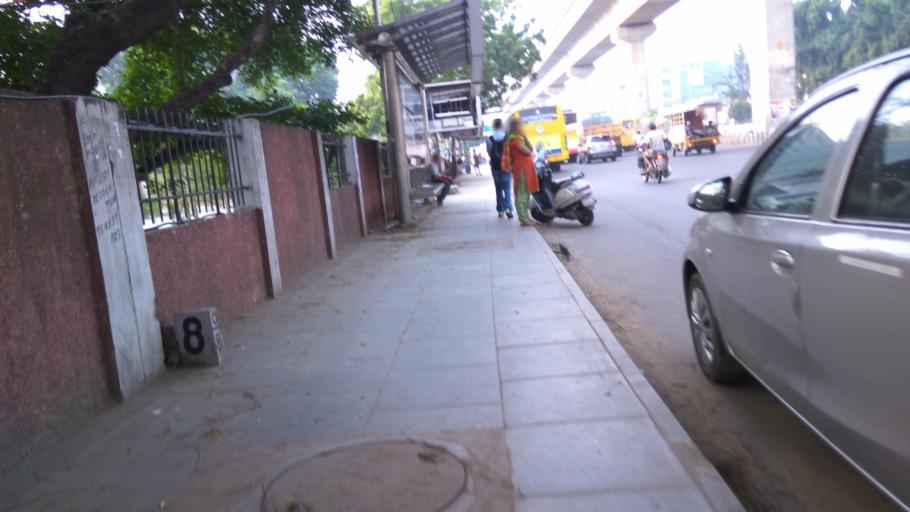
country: IN
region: Tamil Nadu
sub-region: Kancheepuram
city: Alandur
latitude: 13.0148
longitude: 80.2048
